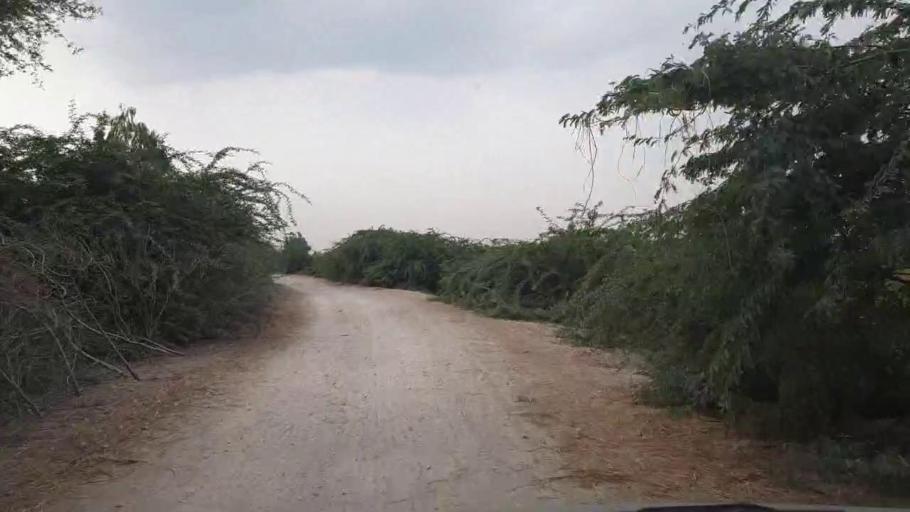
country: PK
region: Sindh
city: Talhar
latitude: 24.9130
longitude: 68.7735
